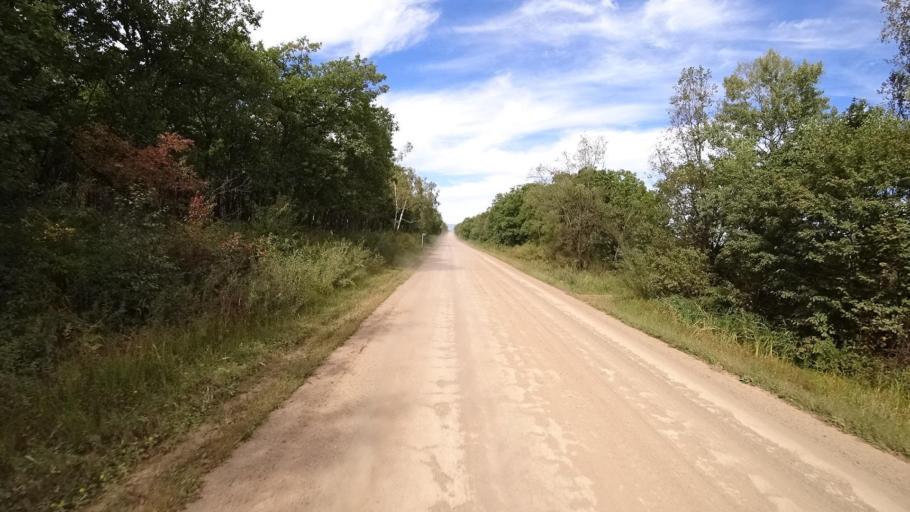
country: RU
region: Primorskiy
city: Yakovlevka
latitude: 44.5992
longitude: 133.6053
